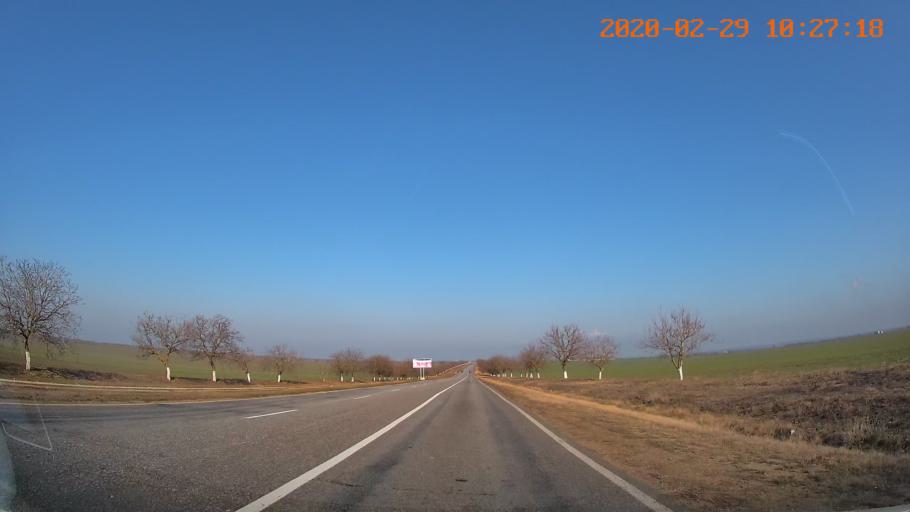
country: MD
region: Telenesti
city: Tiraspolul Nou
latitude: 46.8941
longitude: 29.5986
